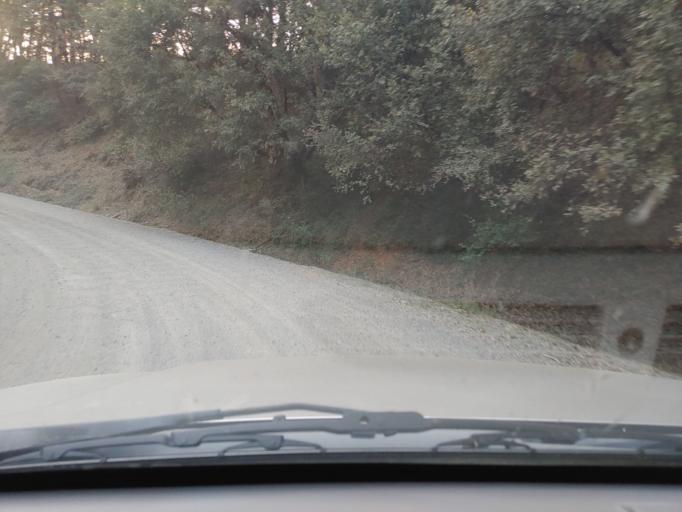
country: US
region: California
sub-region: Shasta County
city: Bella Vista
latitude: 40.8199
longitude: -122.0075
